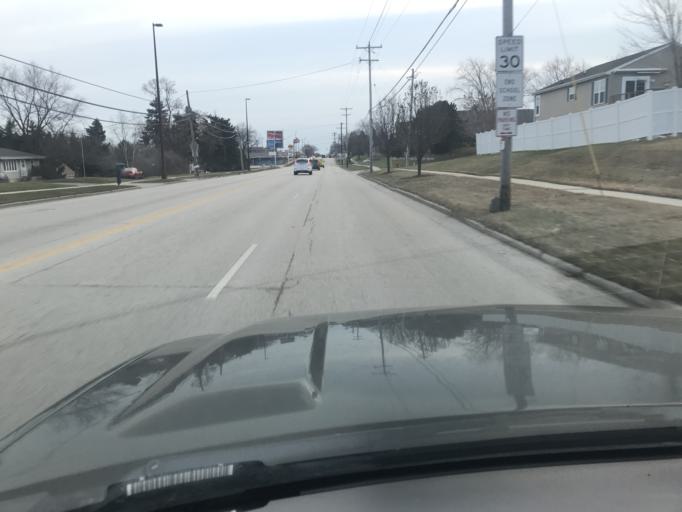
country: US
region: Wisconsin
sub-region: Kenosha County
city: Kenosha
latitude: 42.5885
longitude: -87.8676
